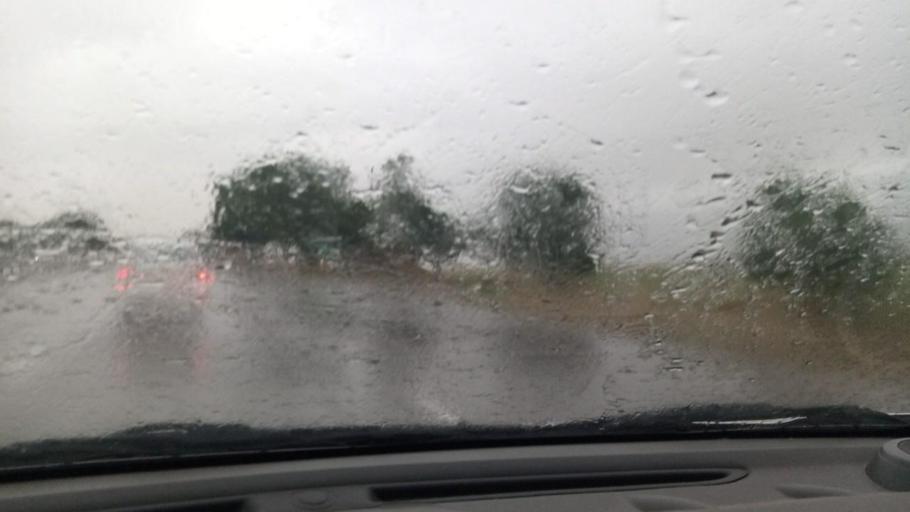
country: UZ
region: Toshkent
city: Ohangaron
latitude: 40.9973
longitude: 69.5287
